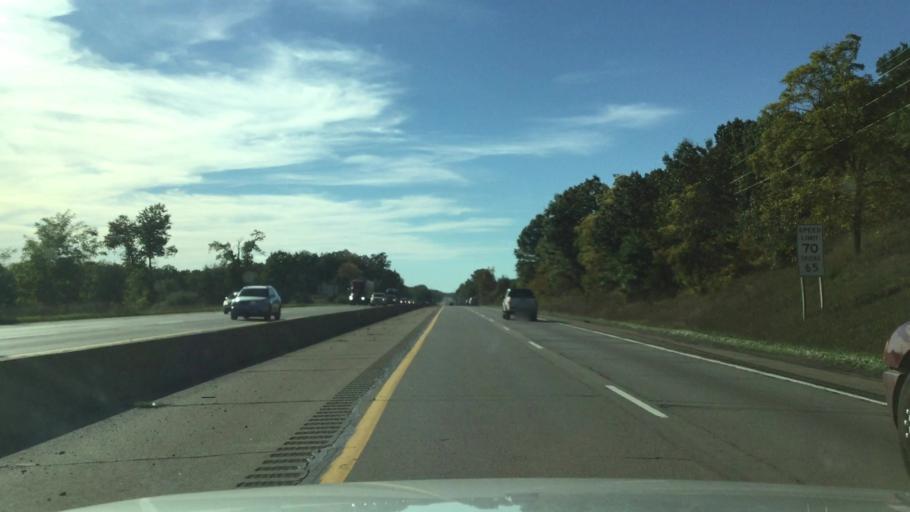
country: US
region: Michigan
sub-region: Jackson County
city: Spring Arbor
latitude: 42.2691
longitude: -84.5496
